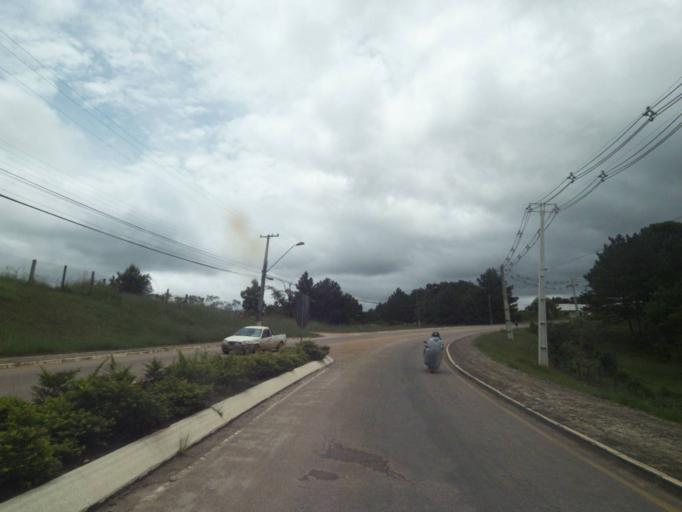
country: BR
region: Parana
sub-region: Campina Grande Do Sul
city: Campina Grande do Sul
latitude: -25.3099
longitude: -49.0612
